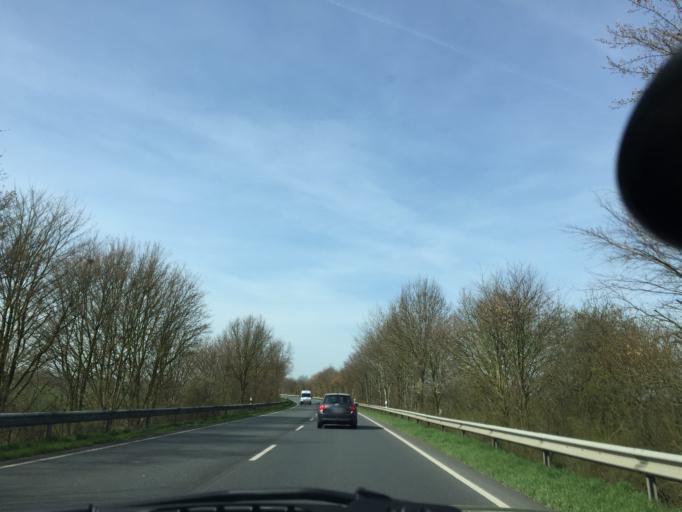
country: DE
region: North Rhine-Westphalia
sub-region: Regierungsbezirk Dusseldorf
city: Goch
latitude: 51.7150
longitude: 6.1500
